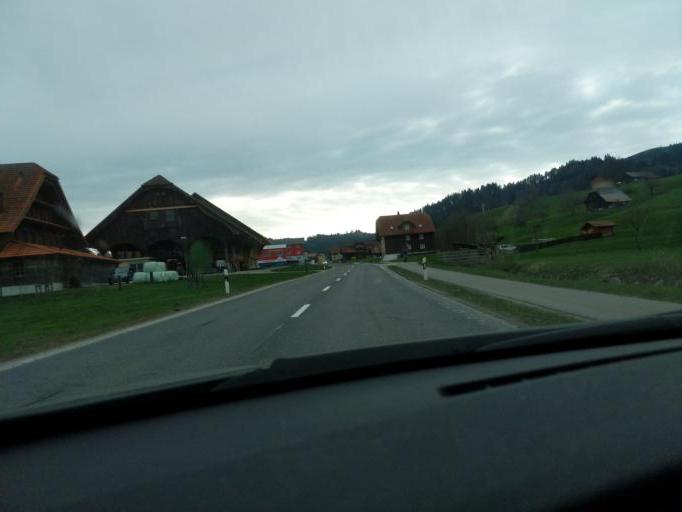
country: CH
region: Lucerne
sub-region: Entlebuch District
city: Escholzmatt
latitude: 46.9239
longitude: 7.9520
